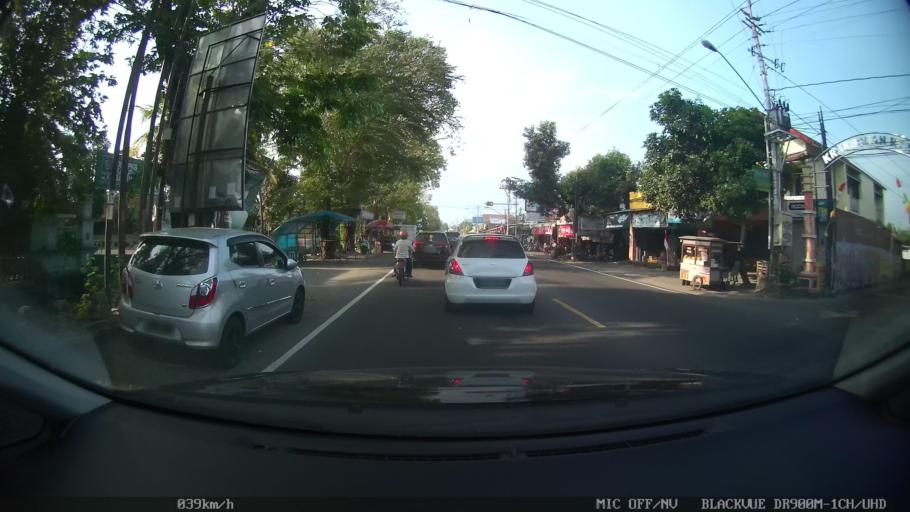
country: ID
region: Daerah Istimewa Yogyakarta
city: Bantul
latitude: -7.8750
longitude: 110.3357
